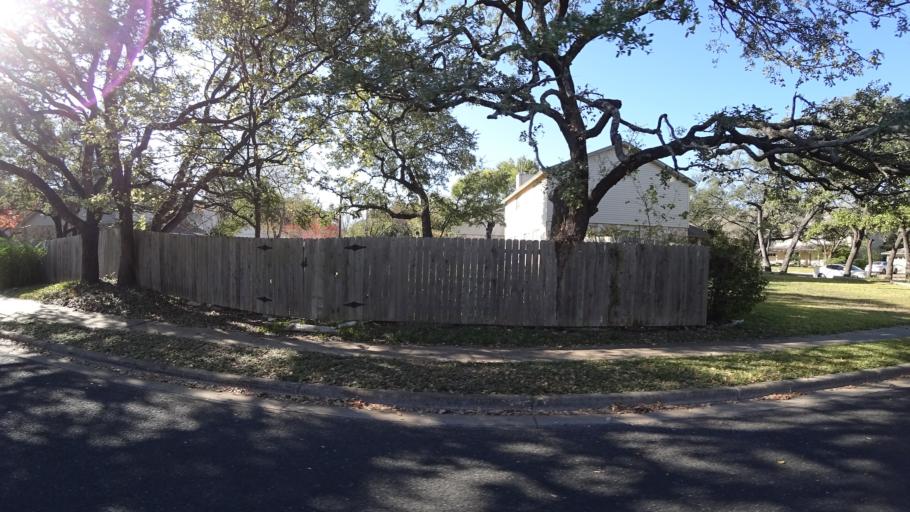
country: US
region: Texas
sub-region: Travis County
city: Shady Hollow
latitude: 30.2253
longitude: -97.8366
